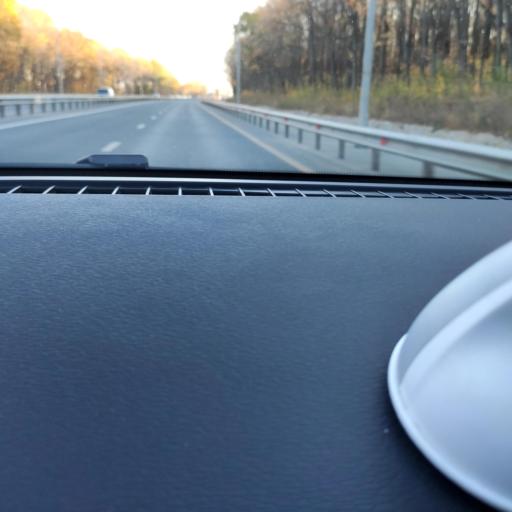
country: RU
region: Samara
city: Petra-Dubrava
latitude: 53.2855
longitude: 50.2508
